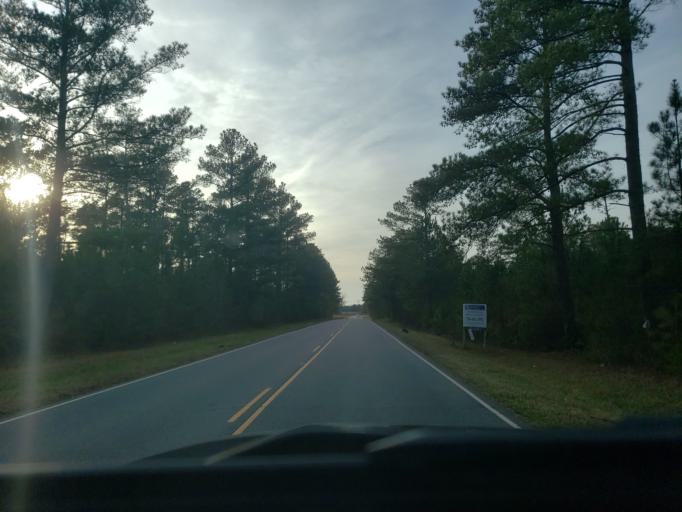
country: US
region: North Carolina
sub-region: Cleveland County
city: Boiling Springs
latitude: 35.3045
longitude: -81.7128
